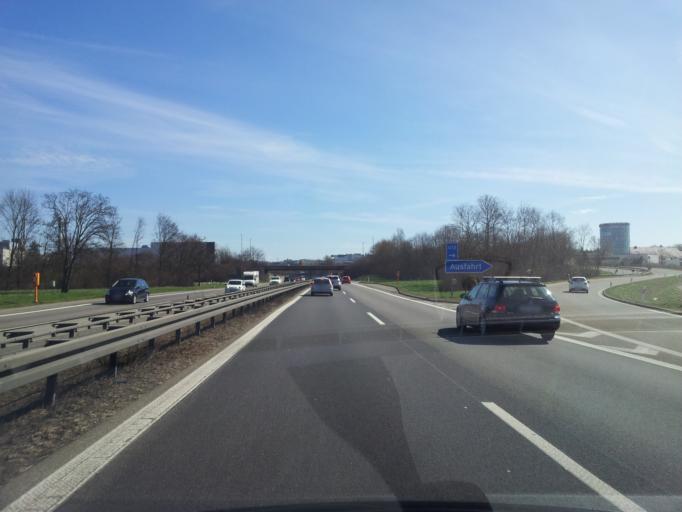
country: DE
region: Baden-Wuerttemberg
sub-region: Regierungsbezirk Stuttgart
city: Boeblingen
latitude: 48.6936
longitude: 8.9990
